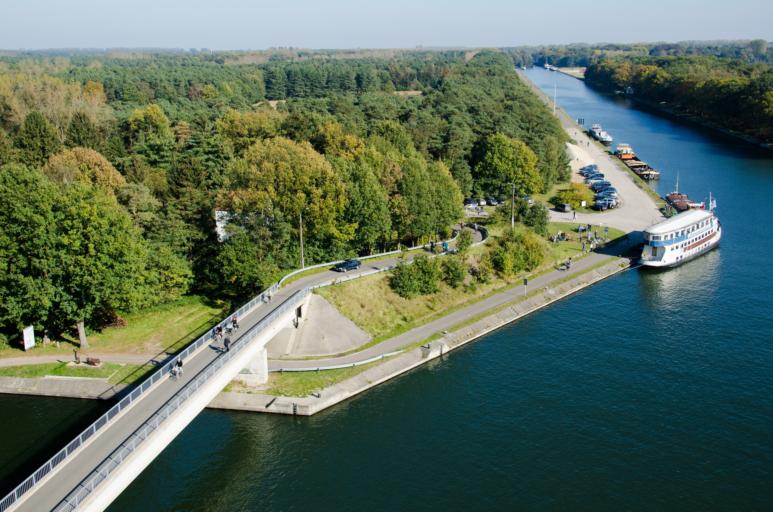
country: BE
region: Flanders
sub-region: Provincie Antwerpen
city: Dessel
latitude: 51.2346
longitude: 5.1637
